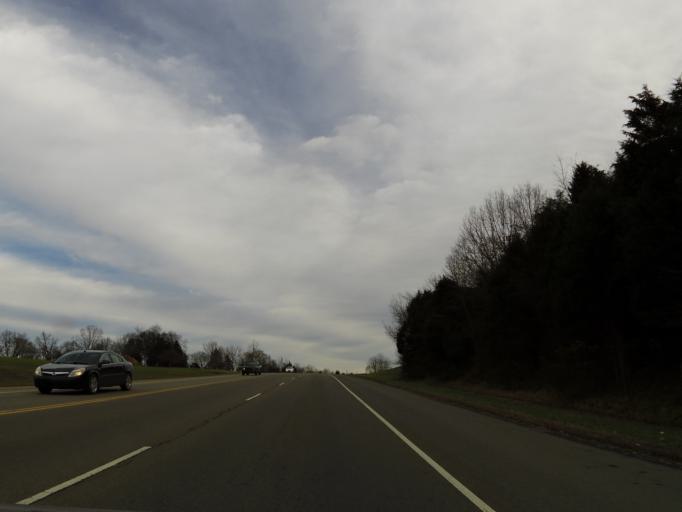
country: US
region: Tennessee
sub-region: Cocke County
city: Newport
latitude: 35.9856
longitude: -83.1551
